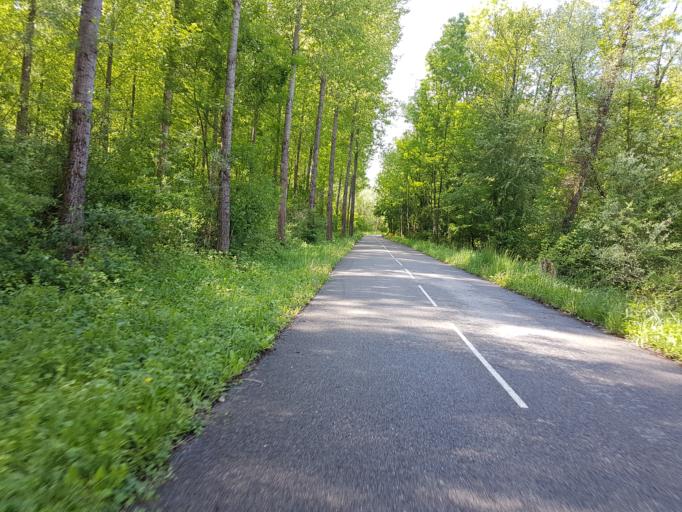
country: FR
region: Rhone-Alpes
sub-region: Departement de l'Ain
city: Culoz
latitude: 45.8630
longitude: 5.8241
